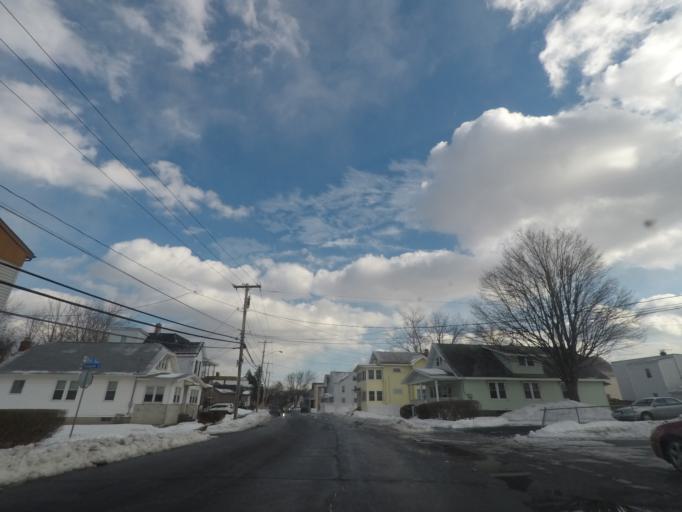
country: US
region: New York
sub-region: Albany County
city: Cohoes
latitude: 42.7779
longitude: -73.7160
